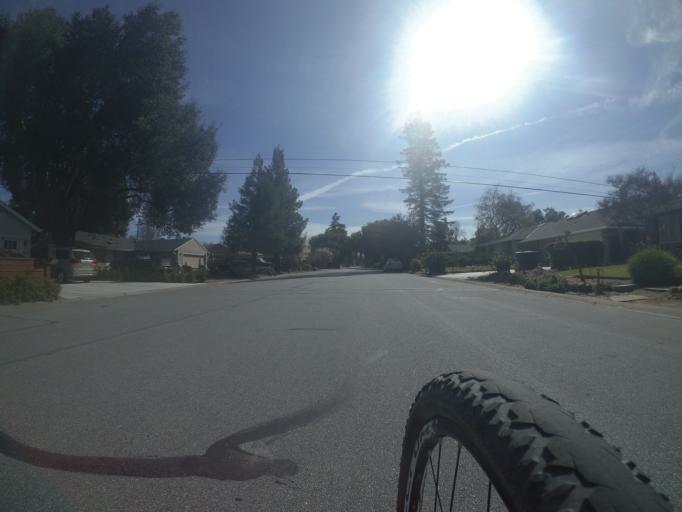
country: US
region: California
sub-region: Santa Clara County
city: Loyola
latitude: 37.3464
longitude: -122.0662
